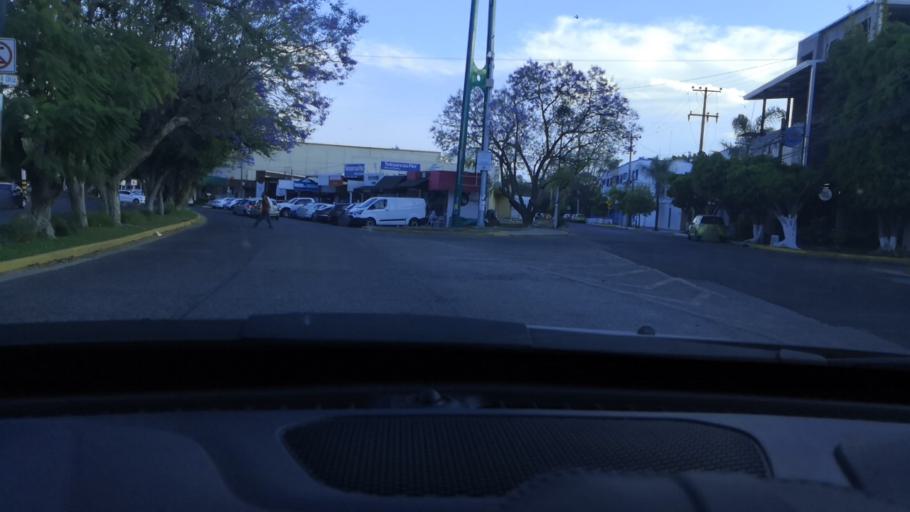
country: MX
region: Jalisco
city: Guadalajara
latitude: 20.6685
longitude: -103.4043
